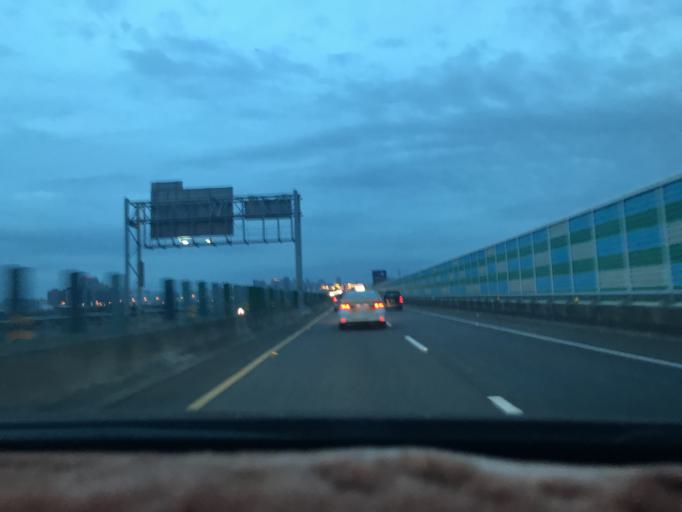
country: TW
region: Taiwan
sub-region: Hsinchu
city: Hsinchu
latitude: 24.8235
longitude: 120.9817
